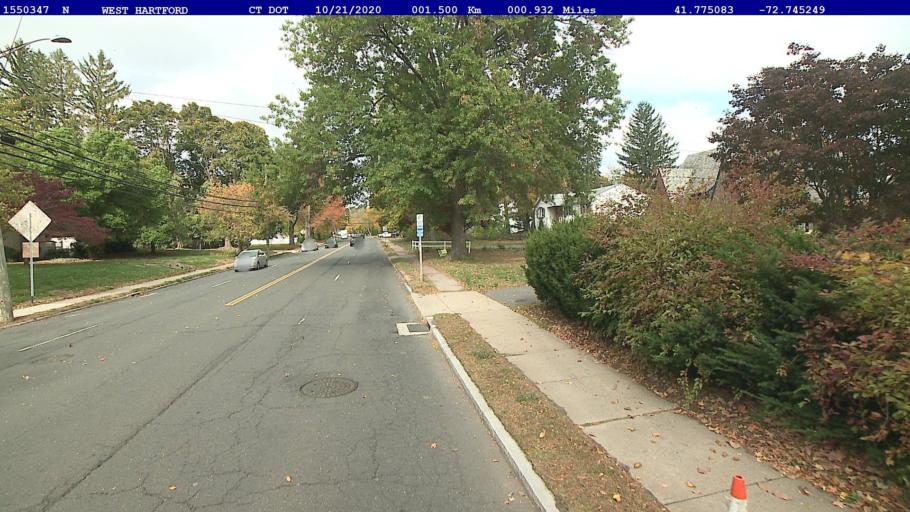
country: US
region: Connecticut
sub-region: Hartford County
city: West Hartford
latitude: 41.7751
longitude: -72.7453
